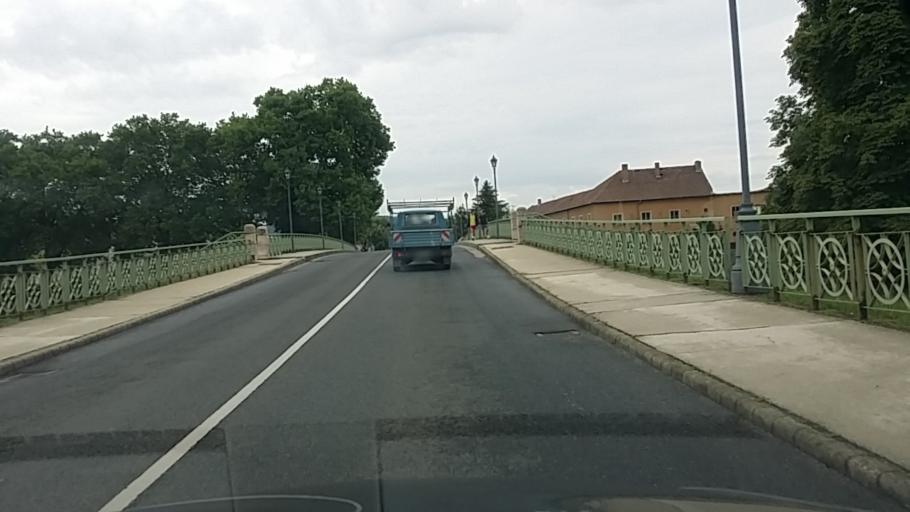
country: HU
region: Komarom-Esztergom
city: Esztergom
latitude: 47.7880
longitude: 18.7338
